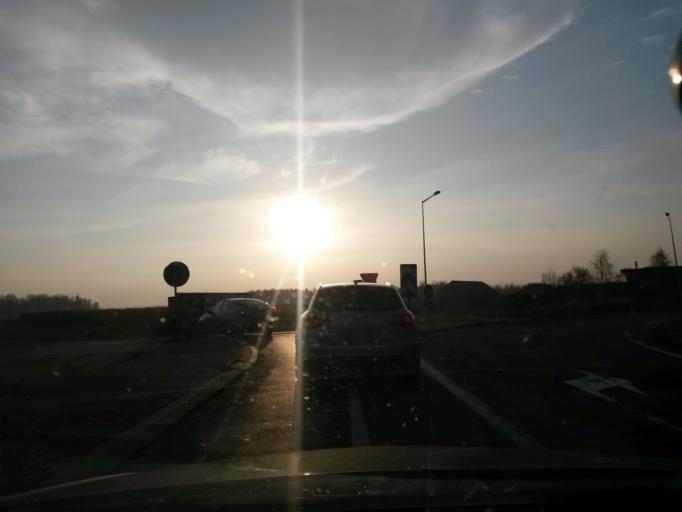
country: PL
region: Lodz Voivodeship
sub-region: Powiat wieruszowski
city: Walichnowy
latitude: 51.3078
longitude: 18.3790
